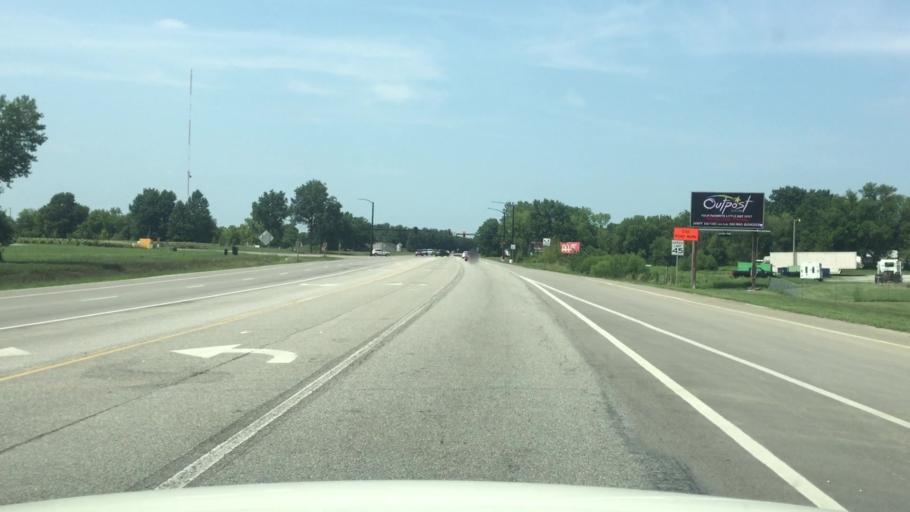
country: US
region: Kansas
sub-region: Crawford County
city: Pittsburg
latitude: 37.3437
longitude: -94.7062
